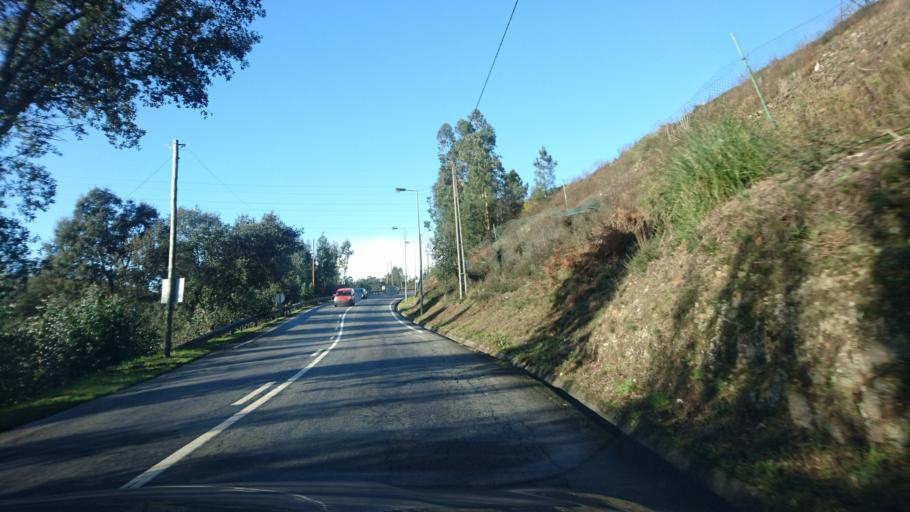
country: PT
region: Porto
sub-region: Paredes
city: Recarei
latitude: 41.1595
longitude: -8.4249
